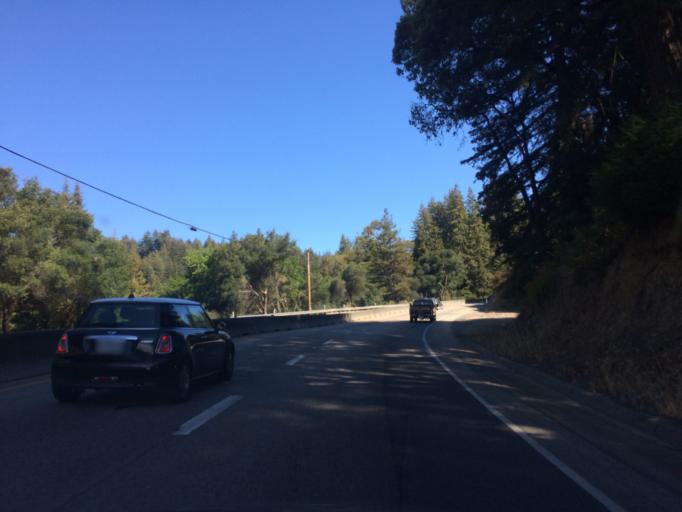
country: US
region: California
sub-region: Santa Cruz County
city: Scotts Valley
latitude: 37.0854
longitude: -121.9783
